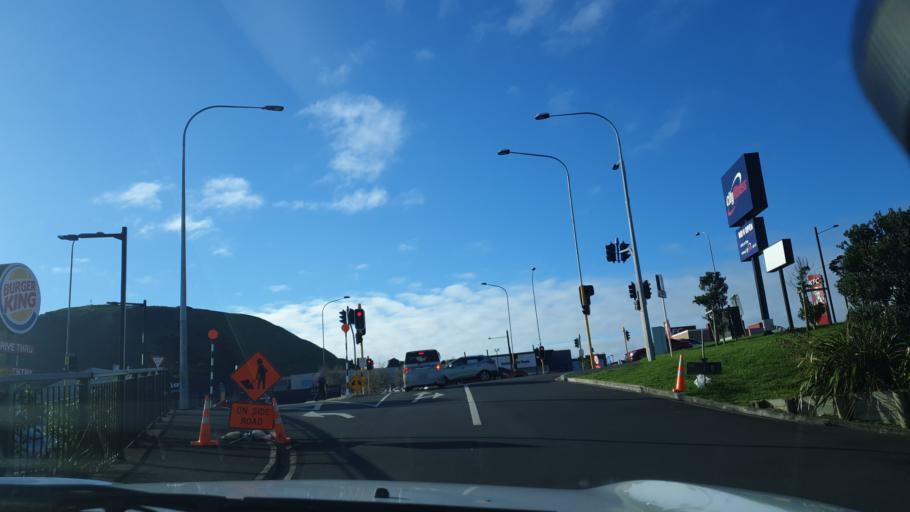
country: NZ
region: Auckland
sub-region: Auckland
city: Tamaki
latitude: -36.8986
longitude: 174.8477
